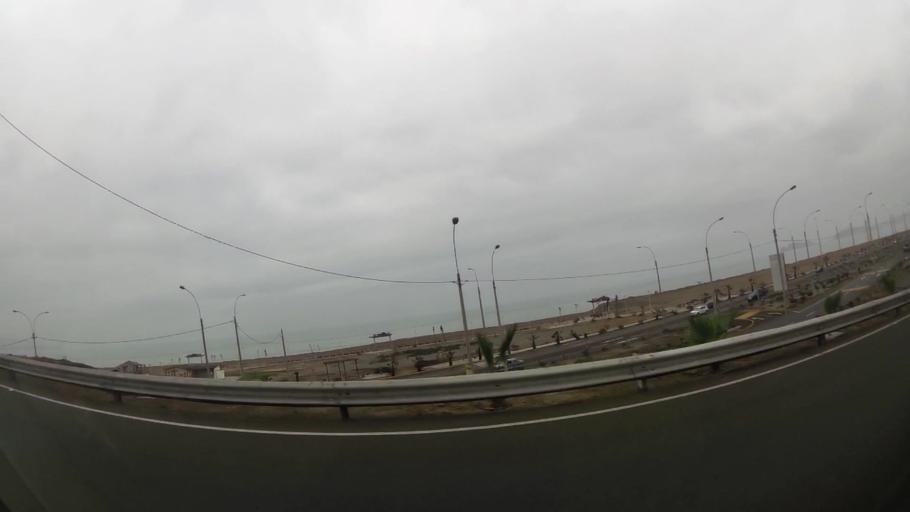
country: PE
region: Lima
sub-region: Lima
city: San Isidro
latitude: -12.0916
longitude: -77.0843
